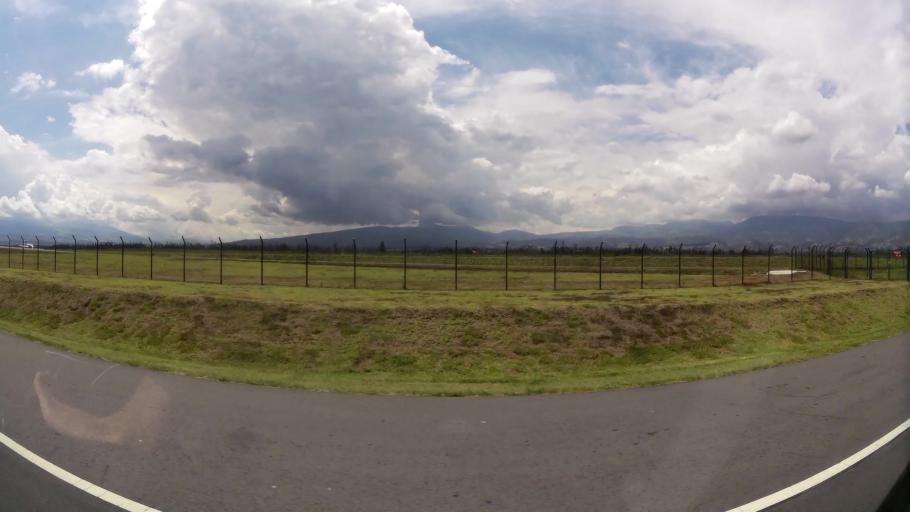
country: EC
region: Pichincha
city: Quito
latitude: -0.1420
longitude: -78.3563
